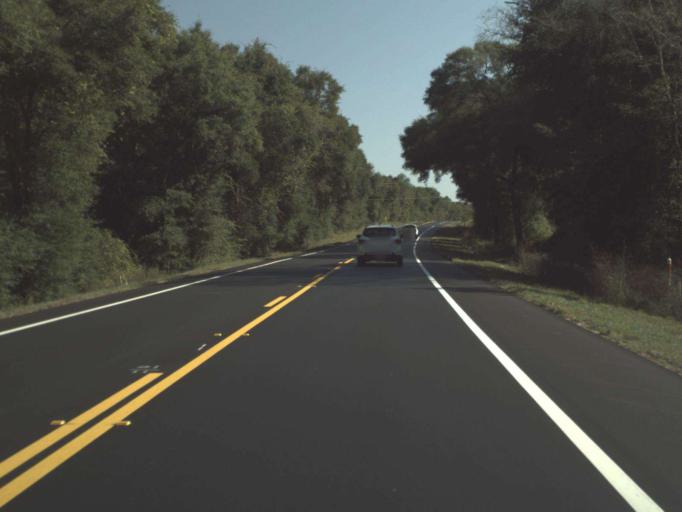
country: US
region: Florida
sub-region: Walton County
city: DeFuniak Springs
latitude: 30.7731
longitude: -86.1576
